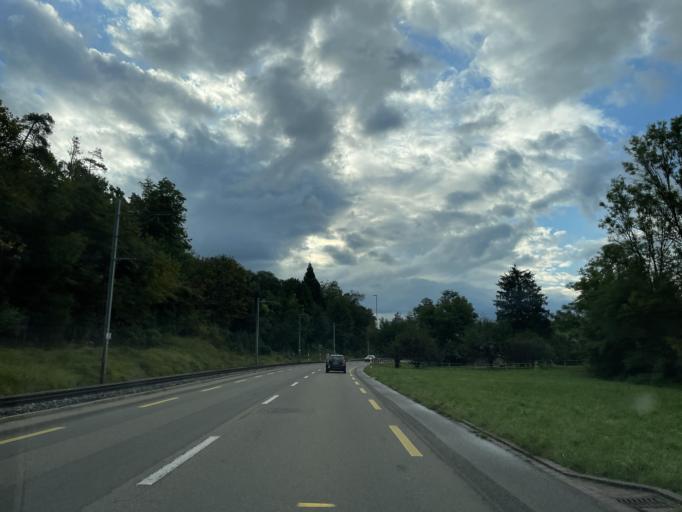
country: CH
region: Thurgau
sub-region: Frauenfeld District
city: Matzingen
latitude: 47.5115
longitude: 8.9418
